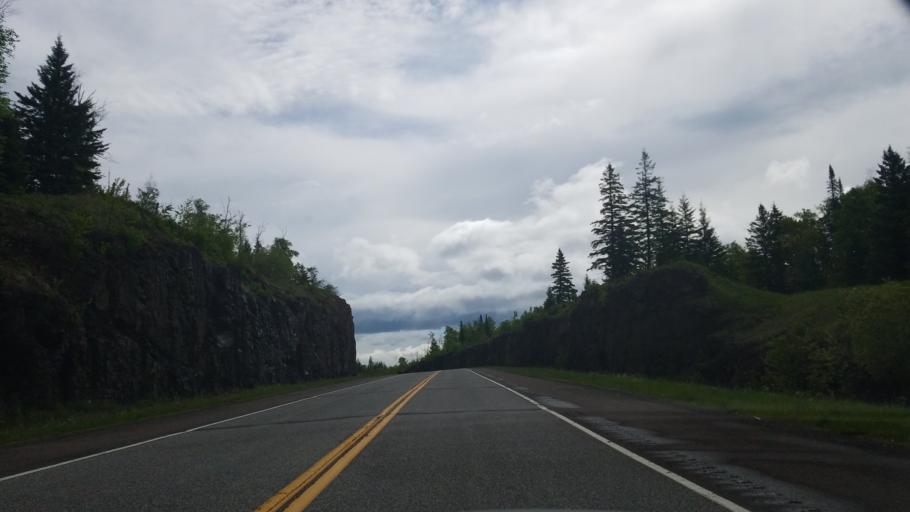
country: US
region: Minnesota
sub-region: Lake County
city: Two Harbors
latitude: 47.1442
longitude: -91.4668
